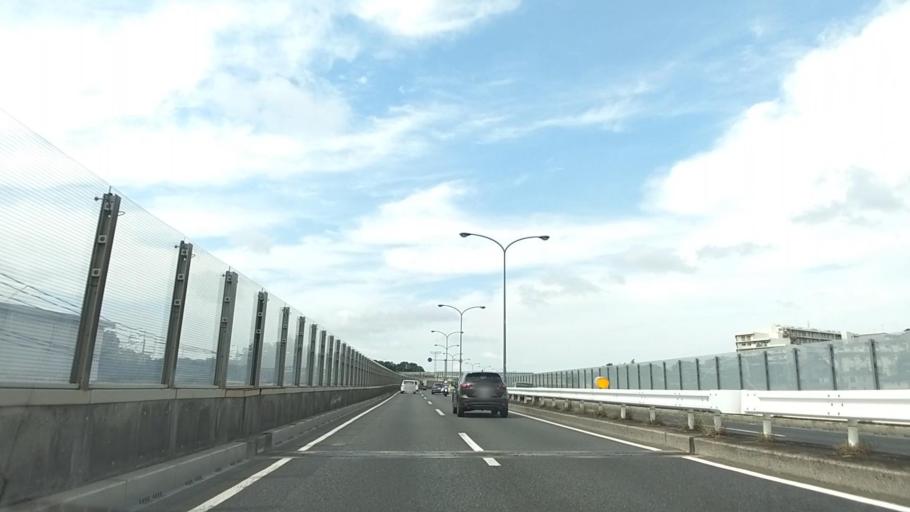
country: JP
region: Kanagawa
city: Yokohama
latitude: 35.4889
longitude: 139.5963
